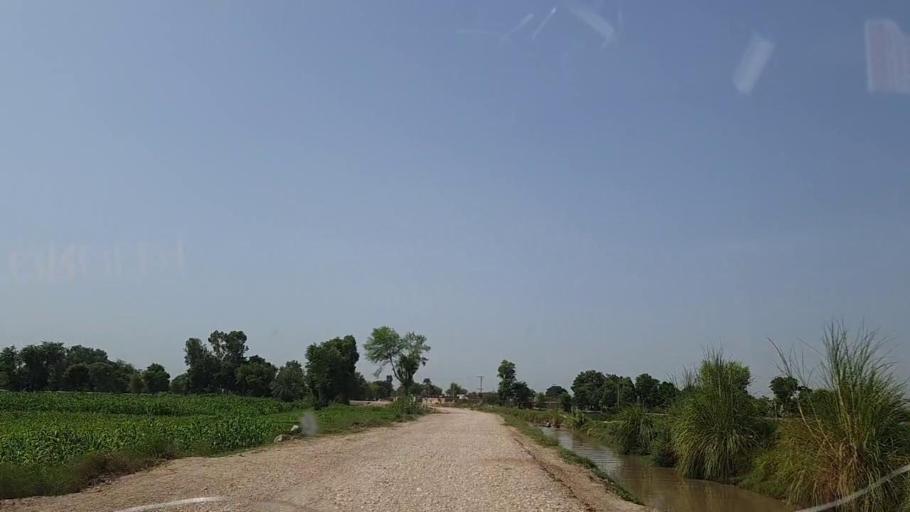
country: PK
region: Sindh
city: Naushahro Firoz
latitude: 26.8541
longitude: 68.0281
